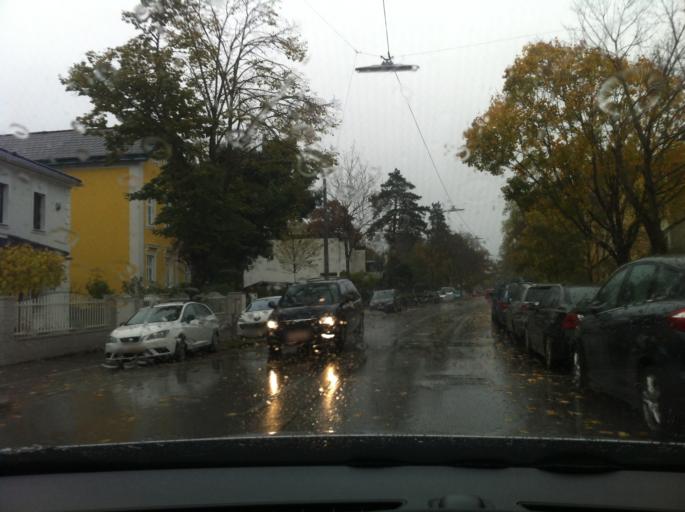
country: AT
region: Lower Austria
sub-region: Politischer Bezirk Wien-Umgebung
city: Purkersdorf
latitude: 48.2101
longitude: 16.2181
